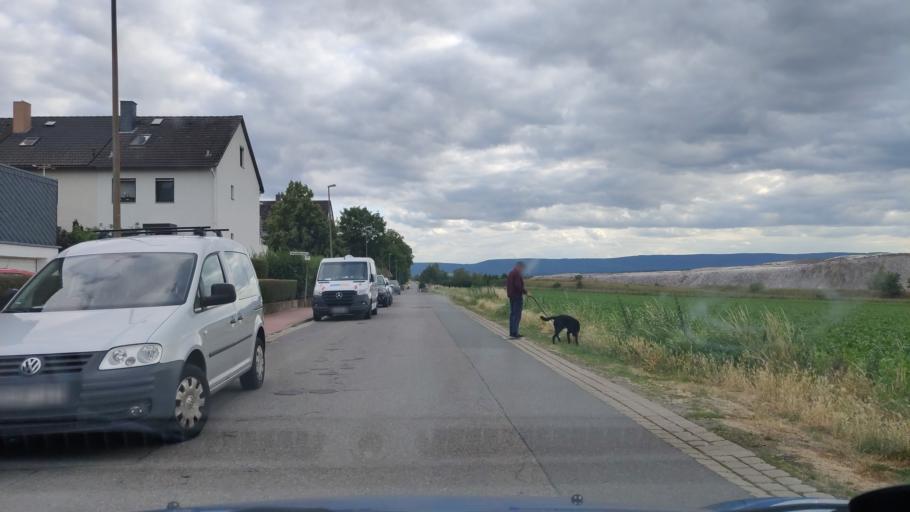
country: DE
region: Lower Saxony
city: Ronnenberg
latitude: 52.3136
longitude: 9.6518
